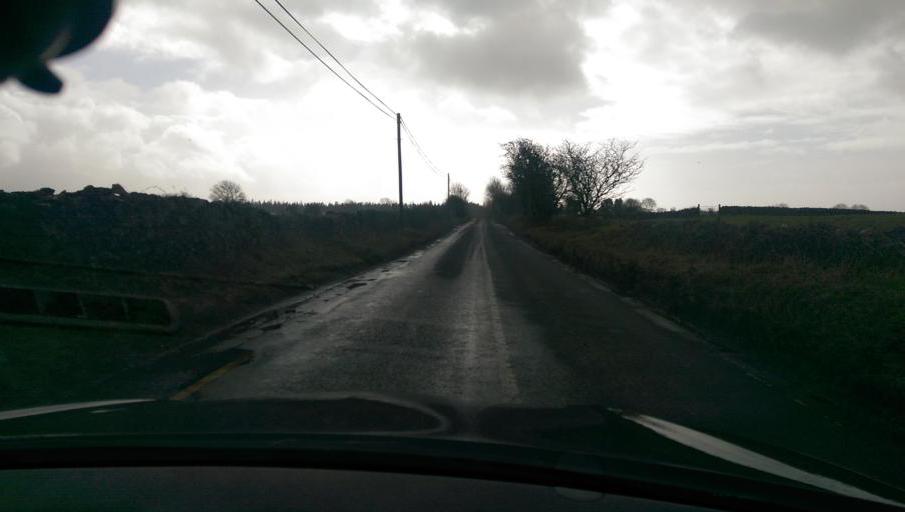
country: IE
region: Connaught
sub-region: County Galway
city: Athenry
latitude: 53.3825
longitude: -8.6943
